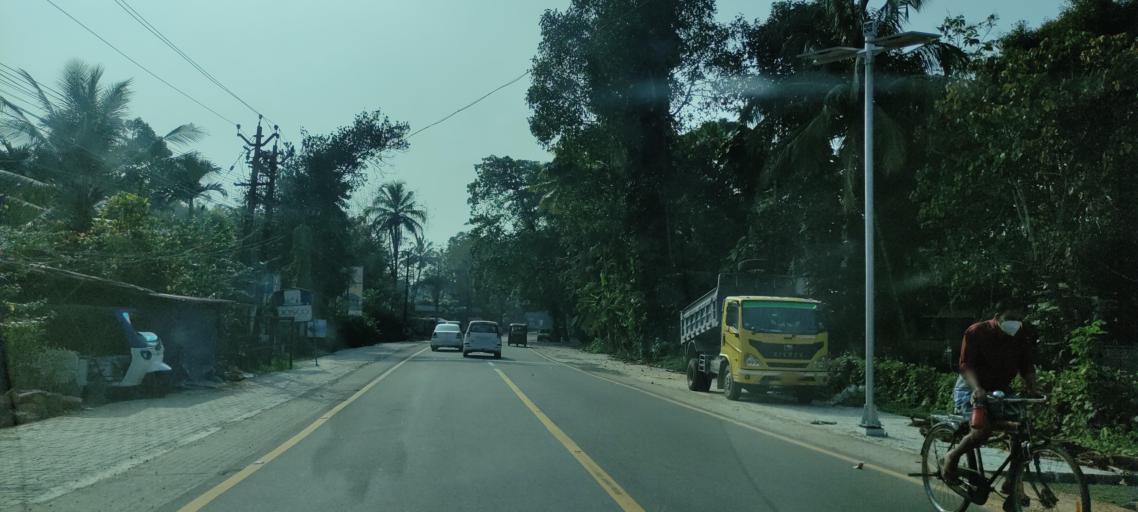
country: IN
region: Kerala
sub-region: Pattanamtitta
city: Tiruvalla
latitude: 9.3679
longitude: 76.5355
